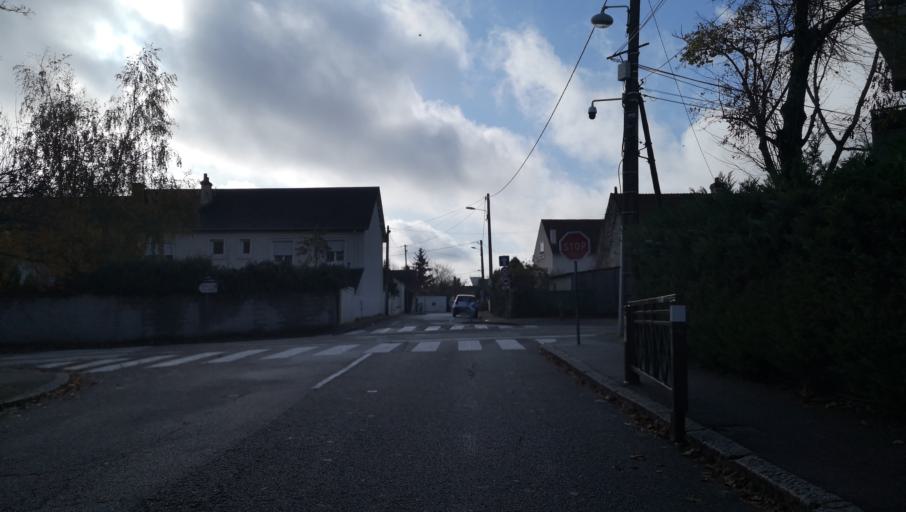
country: FR
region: Centre
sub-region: Departement du Loiret
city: Semoy
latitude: 47.9169
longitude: 1.9375
